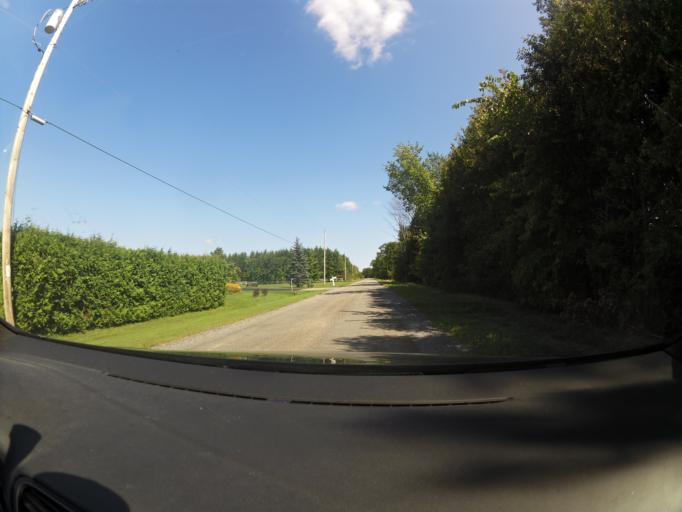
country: CA
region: Ontario
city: Arnprior
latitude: 45.3070
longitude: -76.2632
